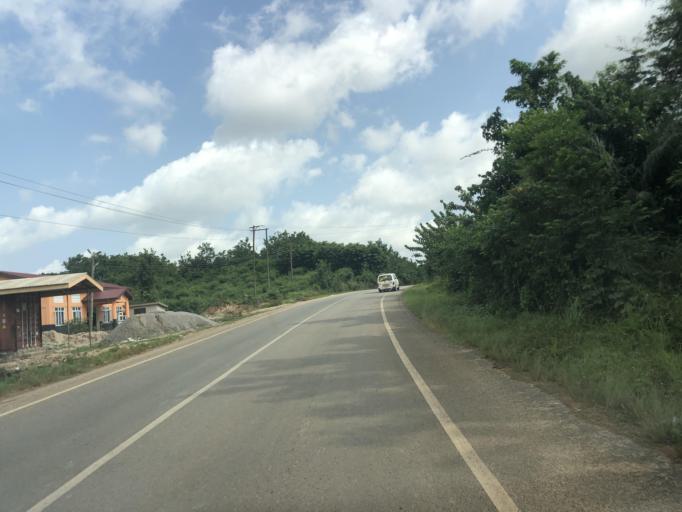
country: GH
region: Central
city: Cape Coast
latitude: 5.1901
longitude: -1.3139
